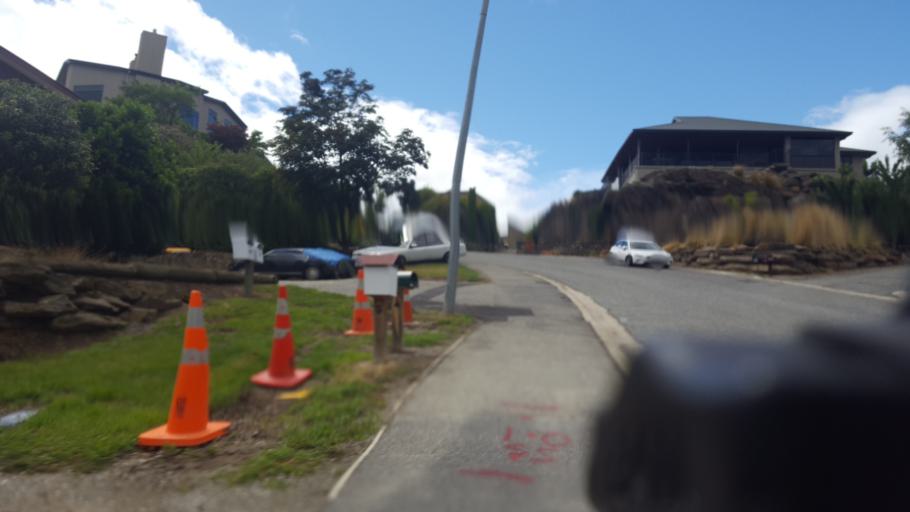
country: NZ
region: Otago
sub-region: Queenstown-Lakes District
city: Wanaka
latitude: -45.2567
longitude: 169.3951
